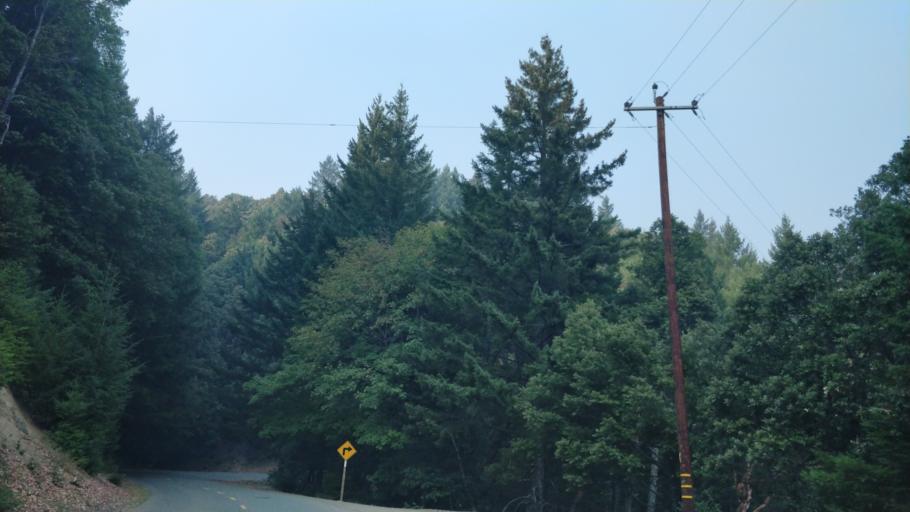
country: US
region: California
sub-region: Humboldt County
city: Rio Dell
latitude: 40.2781
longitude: -124.0698
